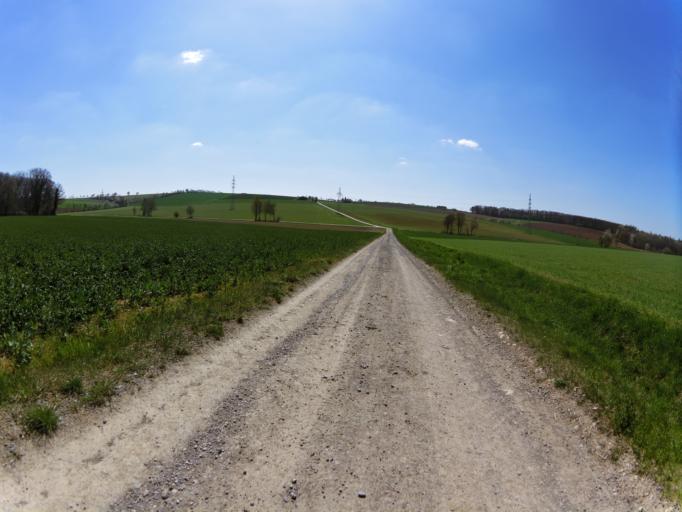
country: DE
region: Bavaria
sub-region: Regierungsbezirk Unterfranken
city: Hettstadt
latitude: 49.8167
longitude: 9.8090
